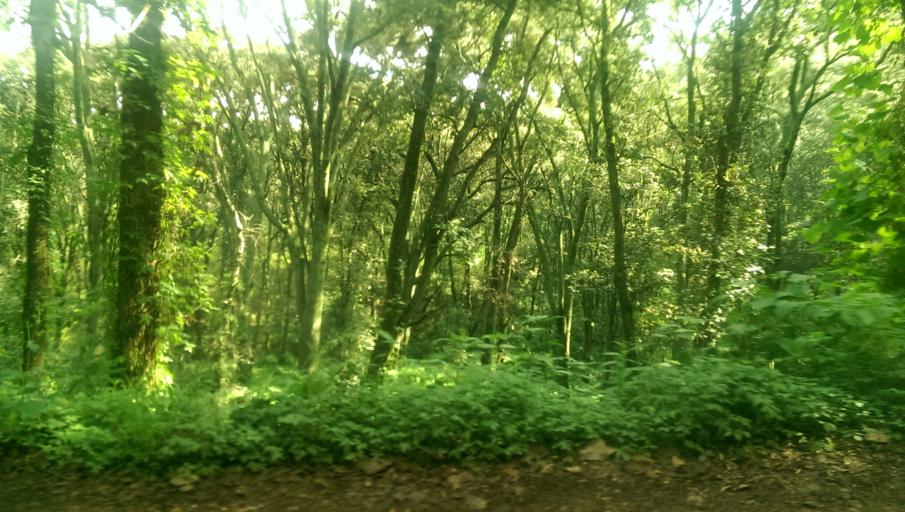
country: MX
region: Mexico
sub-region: Jilotepec
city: Jilotepec de Molina Enriquez
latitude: 19.9220
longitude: -99.4922
